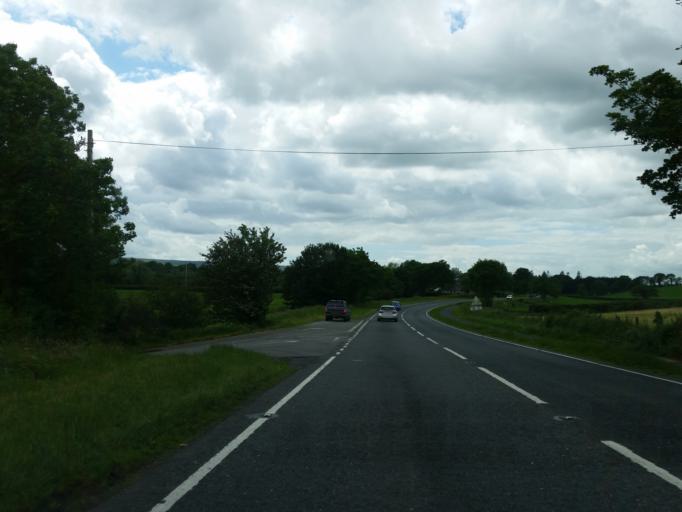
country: GB
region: Northern Ireland
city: Fivemiletown
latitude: 54.4246
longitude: -7.1388
